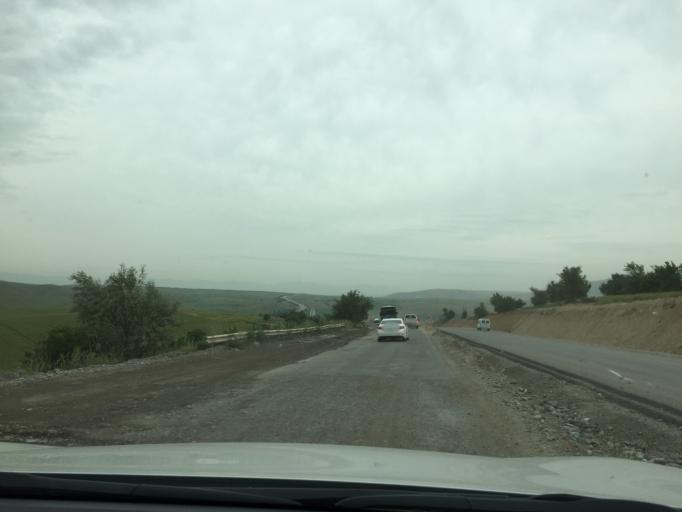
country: KZ
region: Ongtustik Qazaqstan
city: Sastobe
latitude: 42.4894
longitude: 69.9423
